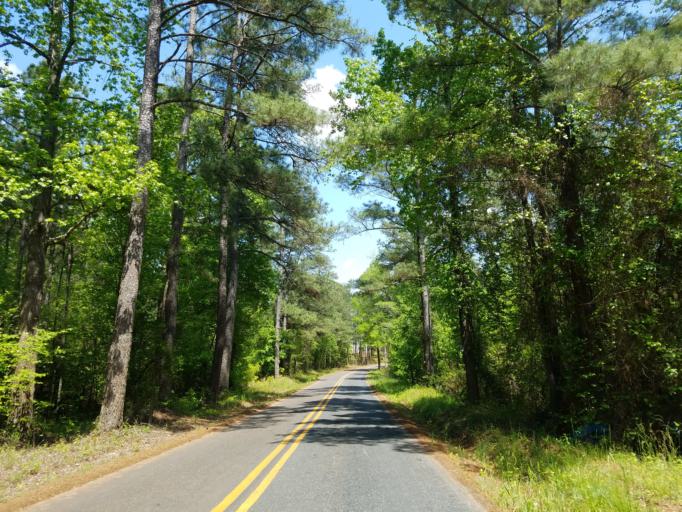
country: US
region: Georgia
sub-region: Monroe County
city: Forsyth
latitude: 33.1417
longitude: -83.9992
